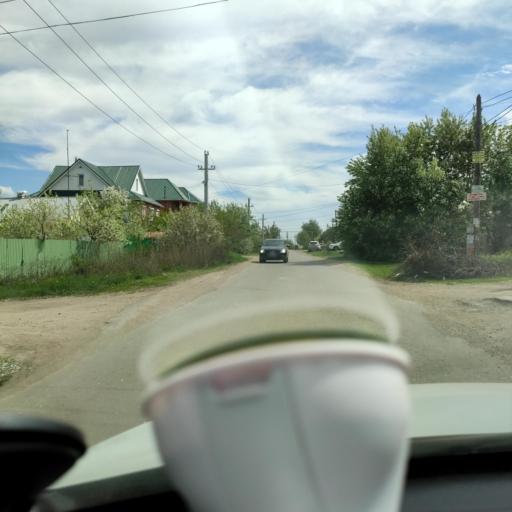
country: RU
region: Samara
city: Petra-Dubrava
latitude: 53.2935
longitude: 50.3097
